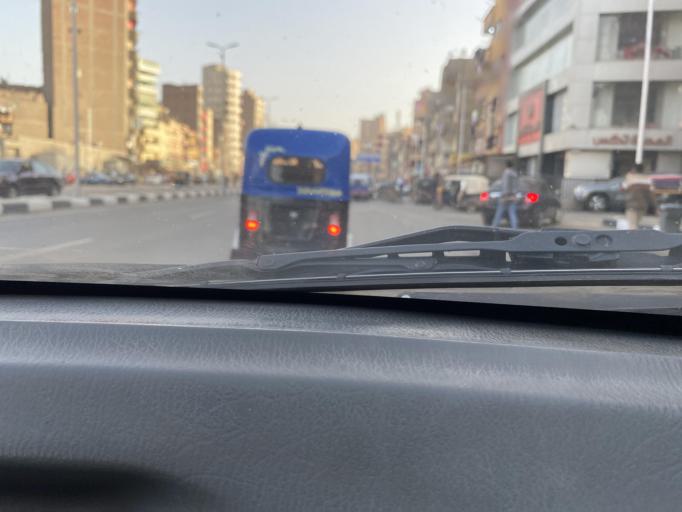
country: EG
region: Muhafazat al Qahirah
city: Cairo
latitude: 30.1243
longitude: 31.2972
